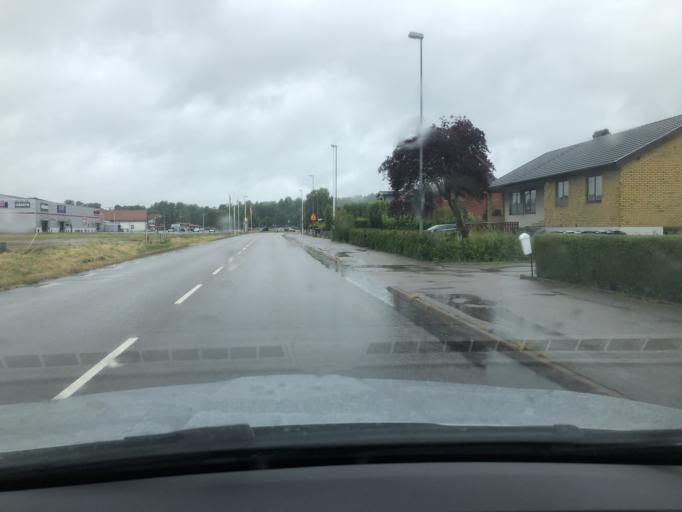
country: SE
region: Blekinge
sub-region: Olofstroms Kommun
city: Olofstroem
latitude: 56.2737
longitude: 14.5326
